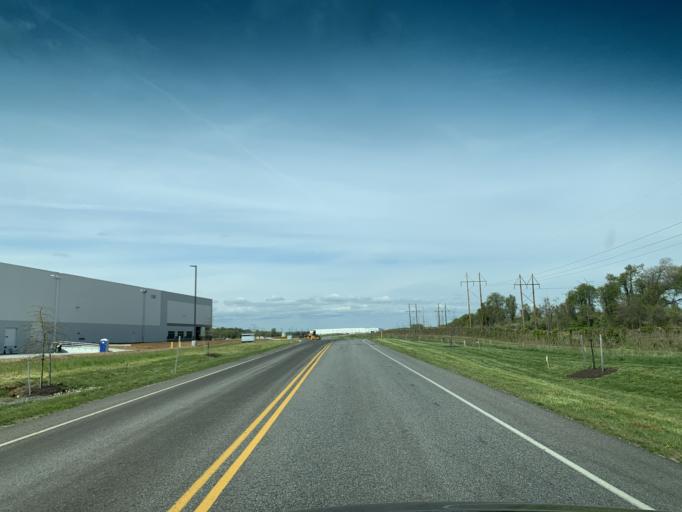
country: US
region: Maryland
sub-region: Harford County
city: Perryman
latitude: 39.4703
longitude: -76.1915
